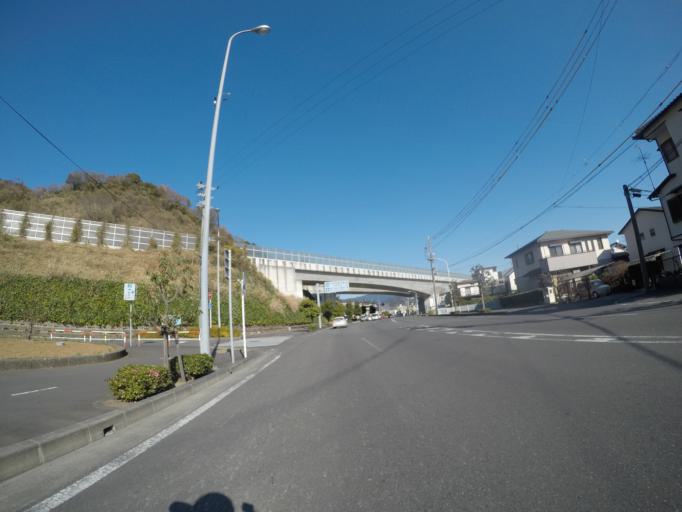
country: JP
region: Shizuoka
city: Shizuoka-shi
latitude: 35.0027
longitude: 138.3810
